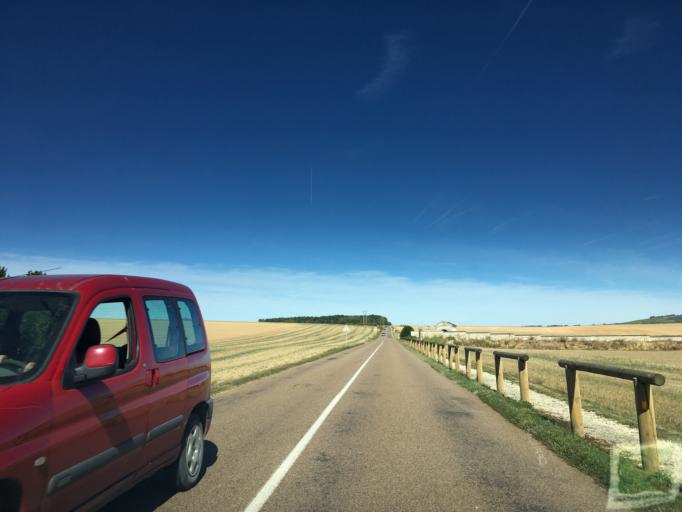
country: FR
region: Bourgogne
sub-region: Departement de l'Yonne
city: Vermenton
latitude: 47.6643
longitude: 3.6623
